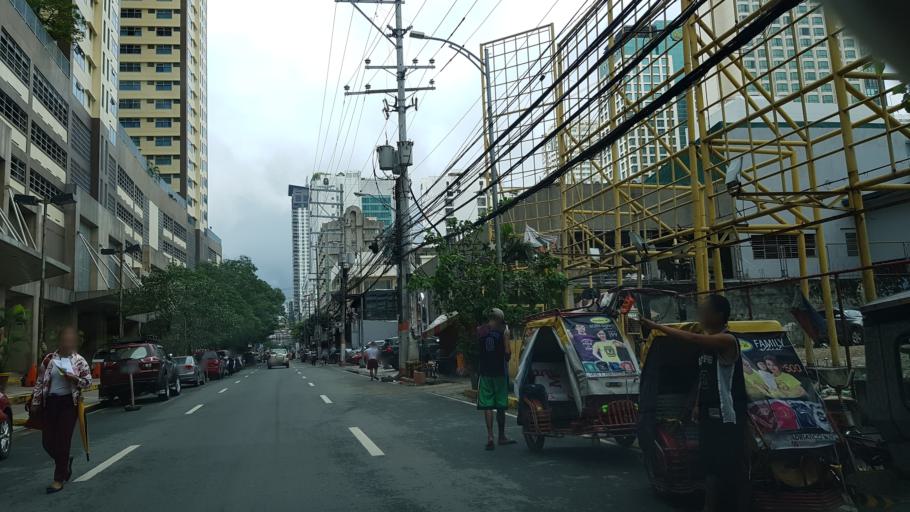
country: PH
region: Metro Manila
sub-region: City of Manila
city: Port Area
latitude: 14.5757
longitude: 120.9830
